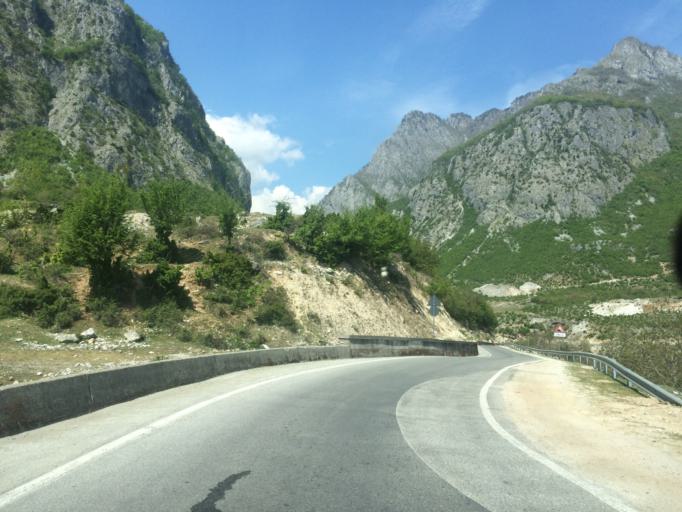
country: AL
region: Kukes
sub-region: Rrethi i Tropojes
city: Bajram Curri
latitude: 42.3851
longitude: 20.0777
